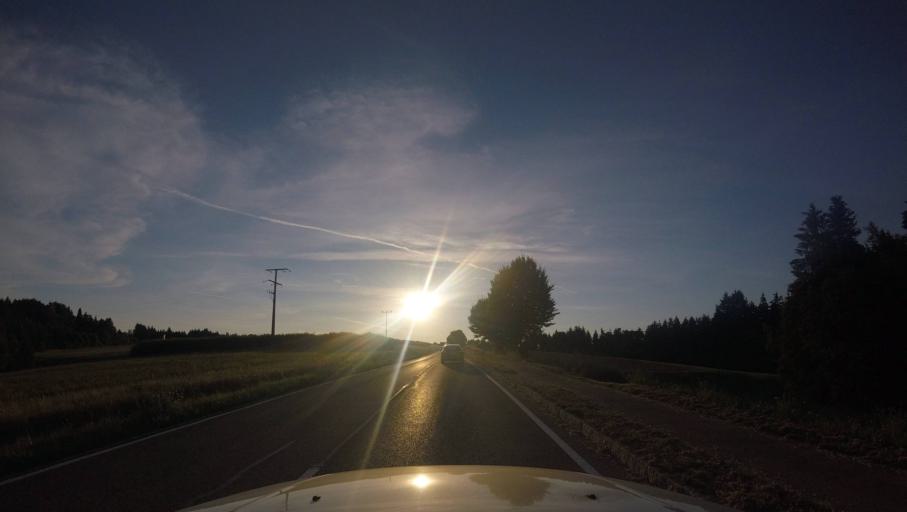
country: DE
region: Baden-Wuerttemberg
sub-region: Regierungsbezirk Stuttgart
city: Kaisersbach
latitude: 48.9198
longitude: 9.6052
